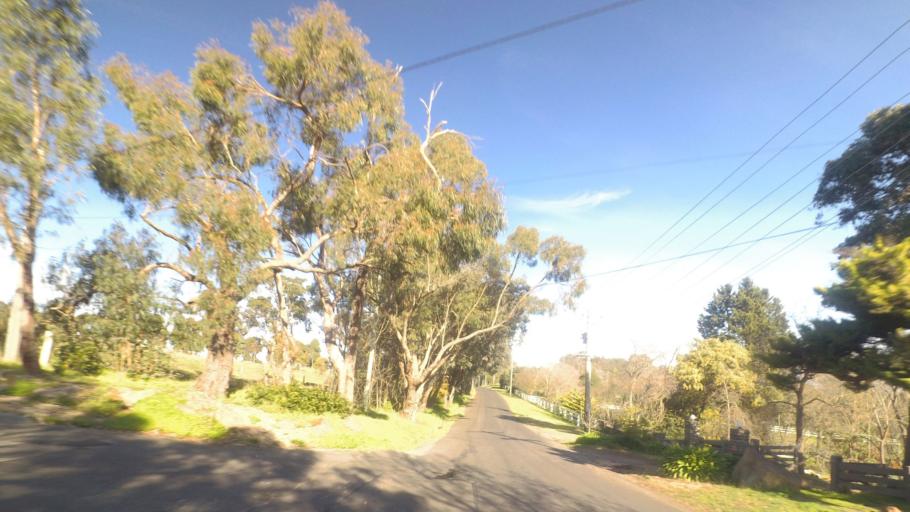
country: AU
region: Victoria
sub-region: Nillumbik
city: Research
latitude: -37.7048
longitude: 145.1944
